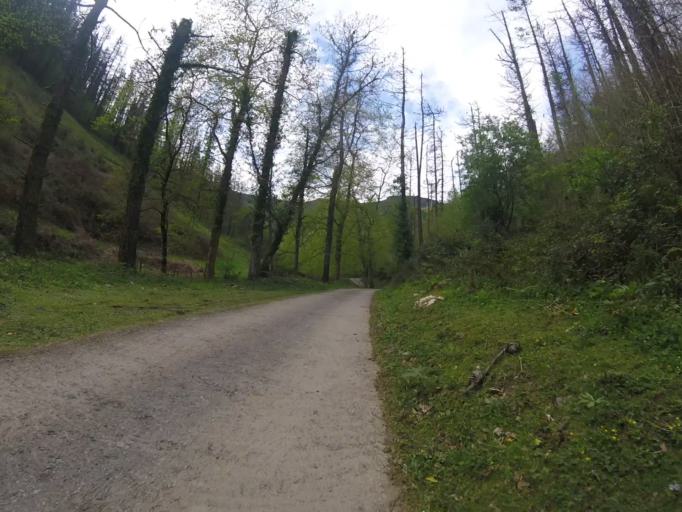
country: ES
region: Basque Country
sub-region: Provincia de Guipuzcoa
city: Errezil
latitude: 43.2043
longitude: -2.1837
